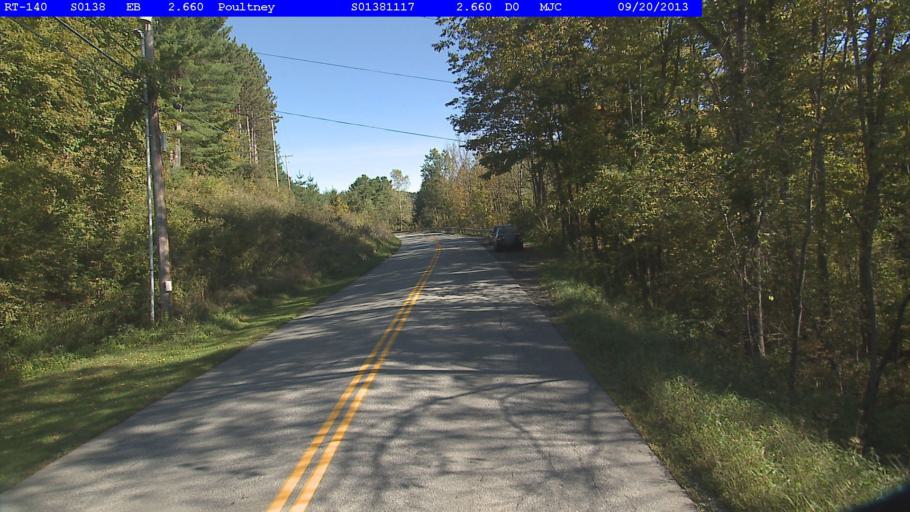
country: US
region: Vermont
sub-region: Rutland County
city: Poultney
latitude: 43.5243
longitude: -73.1862
